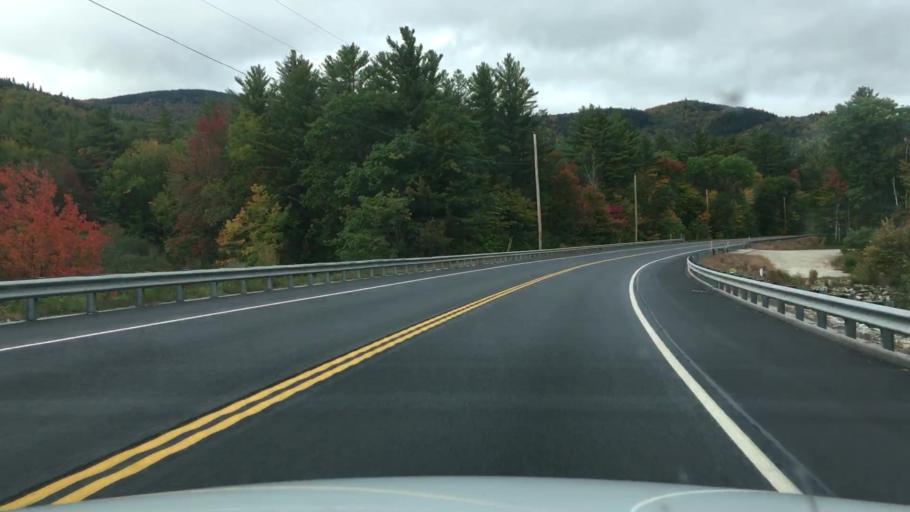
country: US
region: Maine
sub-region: Oxford County
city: Bethel
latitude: 44.3998
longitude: -70.9291
